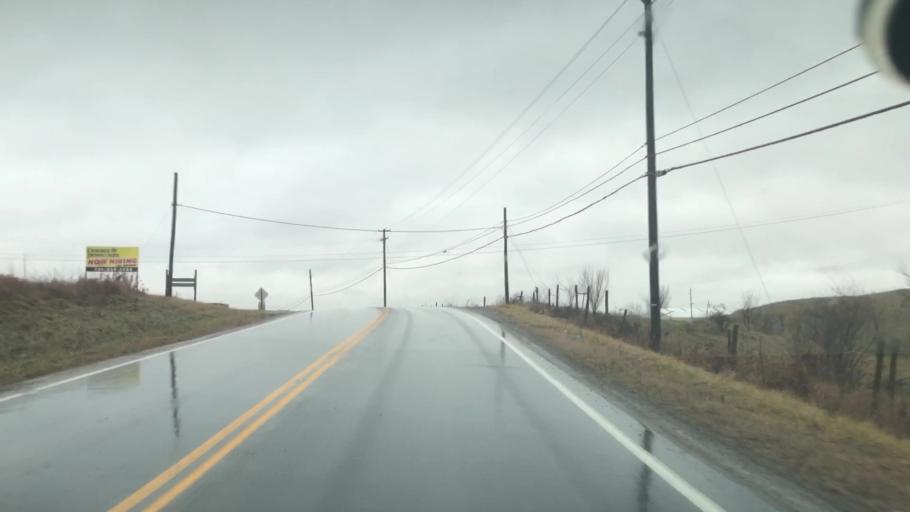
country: US
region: Ohio
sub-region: Harrison County
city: Cadiz
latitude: 40.2464
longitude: -81.0047
